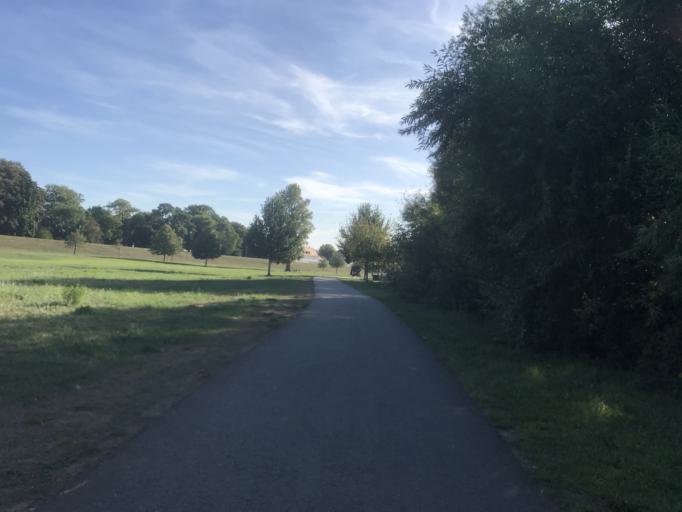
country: DE
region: Hesse
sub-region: Regierungsbezirk Darmstadt
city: Russelsheim
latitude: 49.9994
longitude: 8.4159
